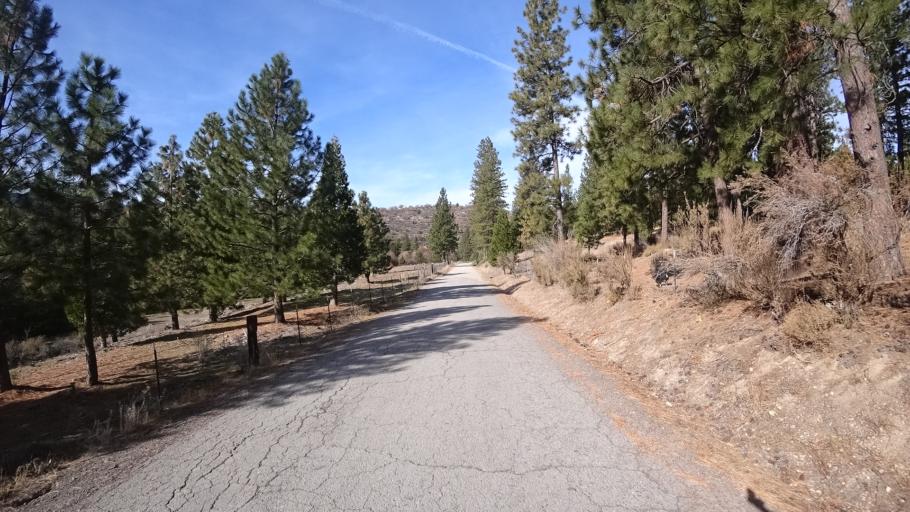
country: US
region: California
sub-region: Siskiyou County
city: Weed
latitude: 41.4333
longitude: -122.4217
